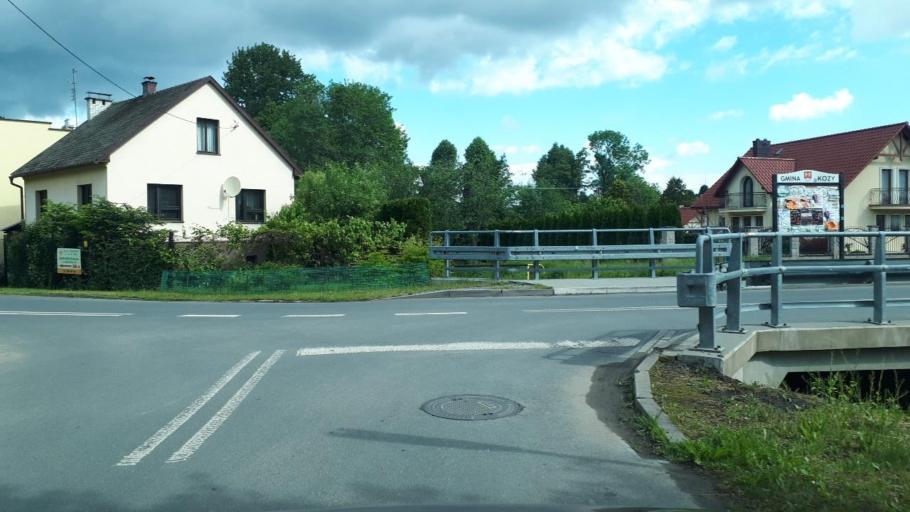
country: PL
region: Silesian Voivodeship
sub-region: Powiat bielski
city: Kozy
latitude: 49.8593
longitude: 19.1257
